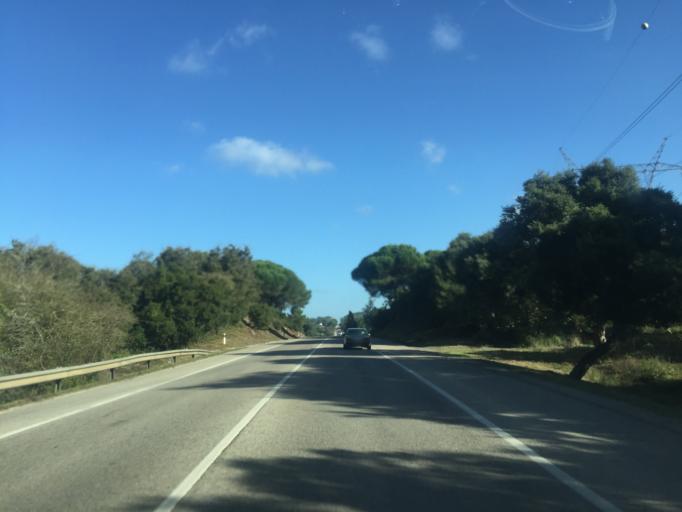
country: PT
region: Leiria
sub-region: Alcobaca
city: Turquel
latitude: 39.4705
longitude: -8.9411
